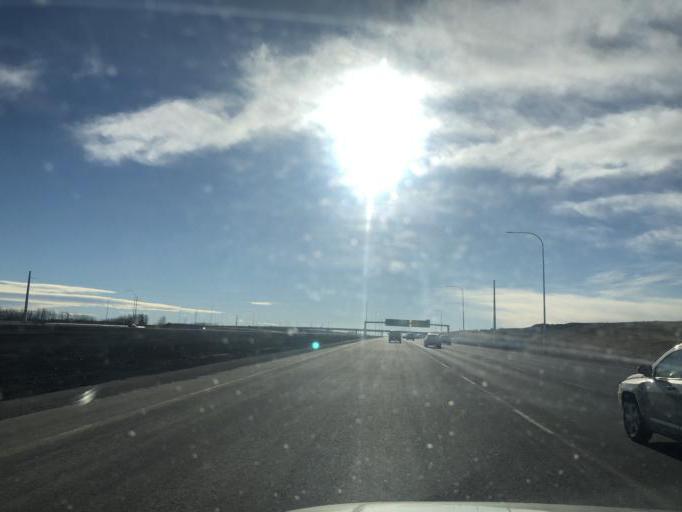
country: CA
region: Alberta
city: Calgary
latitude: 50.9828
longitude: -114.1637
